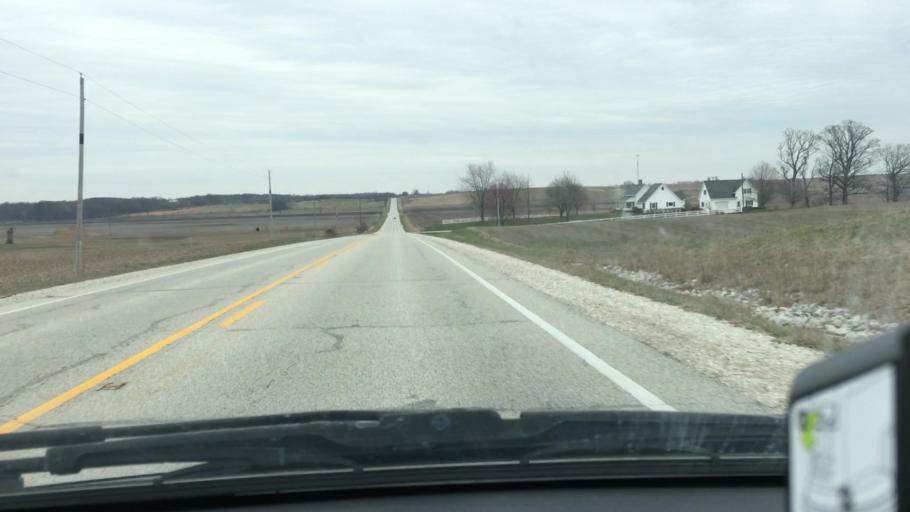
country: US
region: Indiana
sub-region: Greene County
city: Bloomfield
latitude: 38.9972
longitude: -87.0163
